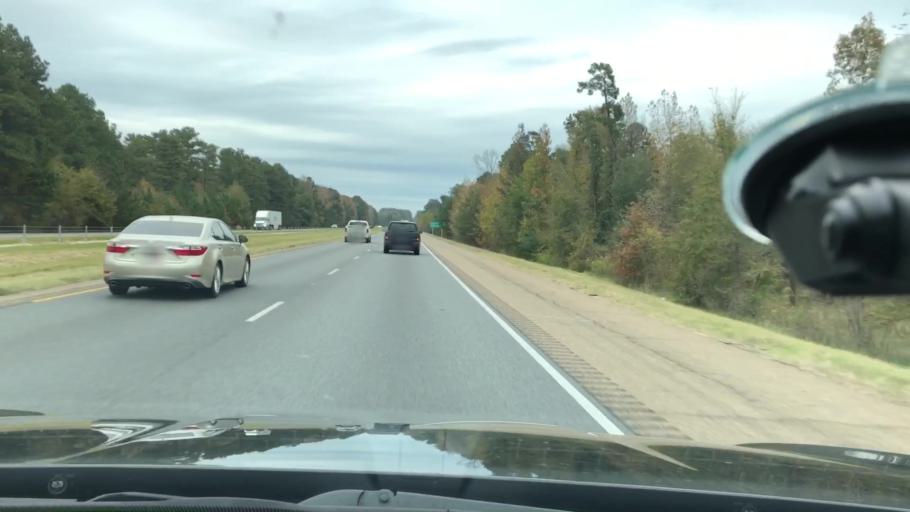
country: US
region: Arkansas
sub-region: Clark County
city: Gurdon
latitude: 33.9093
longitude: -93.2886
